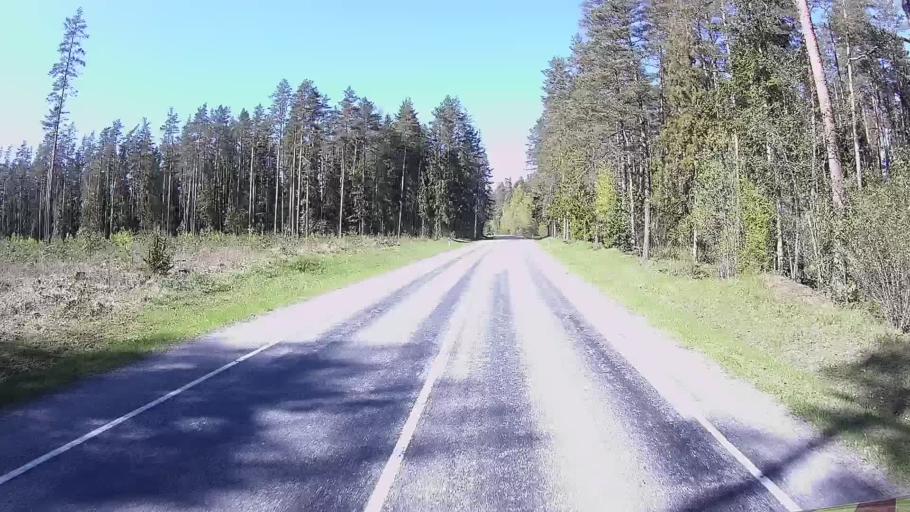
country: EE
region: Laeaene-Virumaa
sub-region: Tapa vald
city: Tapa
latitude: 59.4207
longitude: 25.9909
